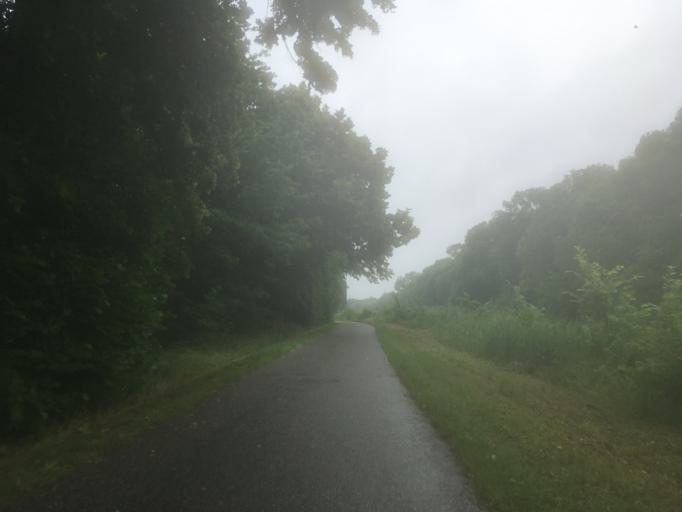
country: DE
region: Brandenburg
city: Zehdenick
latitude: 52.9697
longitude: 13.3493
